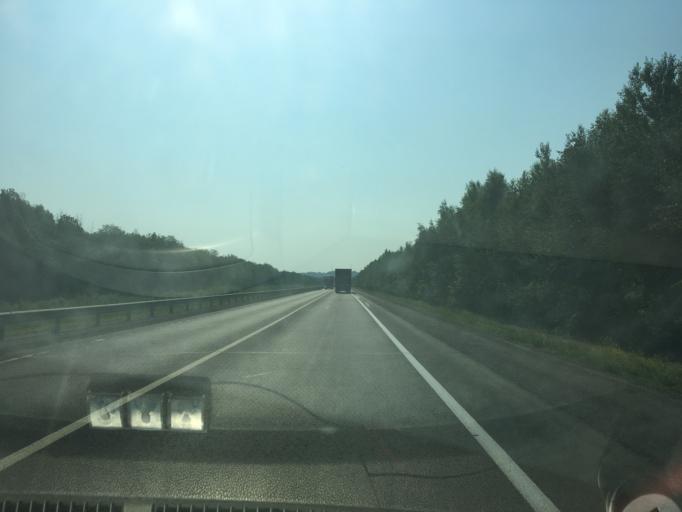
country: RU
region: Nizjnij Novgorod
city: Pamyat' Parizhskoy Kommuny
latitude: 56.0834
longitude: 44.3527
